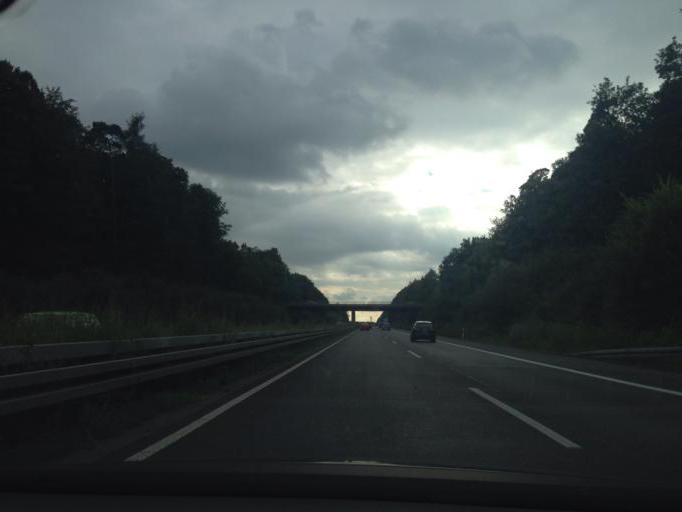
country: DE
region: Hesse
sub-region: Regierungsbezirk Giessen
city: Giessen
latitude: 50.5594
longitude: 8.6832
